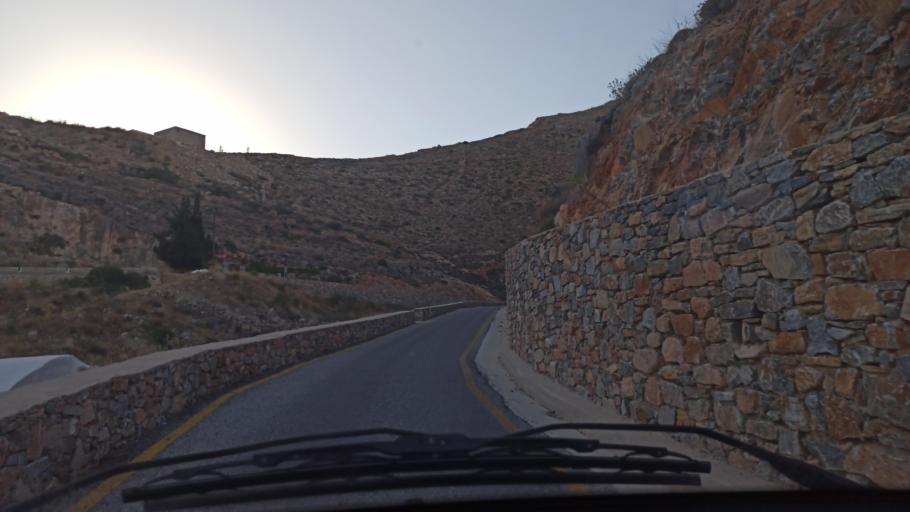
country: GR
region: South Aegean
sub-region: Nomos Kykladon
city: Ano Syros
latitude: 37.4540
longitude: 24.9359
